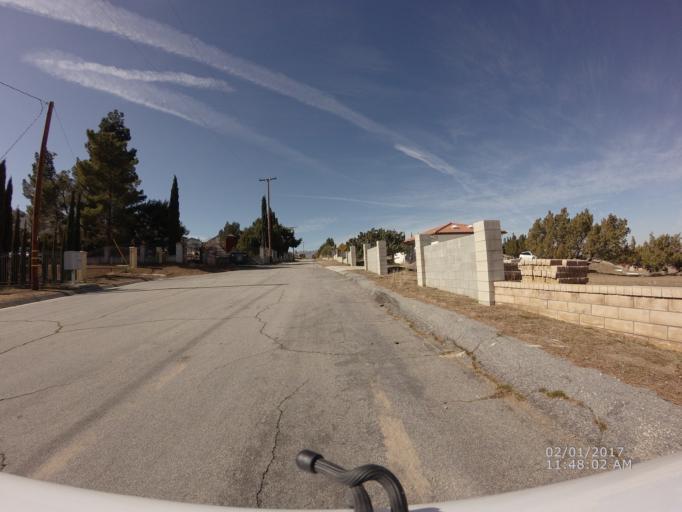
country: US
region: California
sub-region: Los Angeles County
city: Palmdale
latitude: 34.5459
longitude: -118.1258
